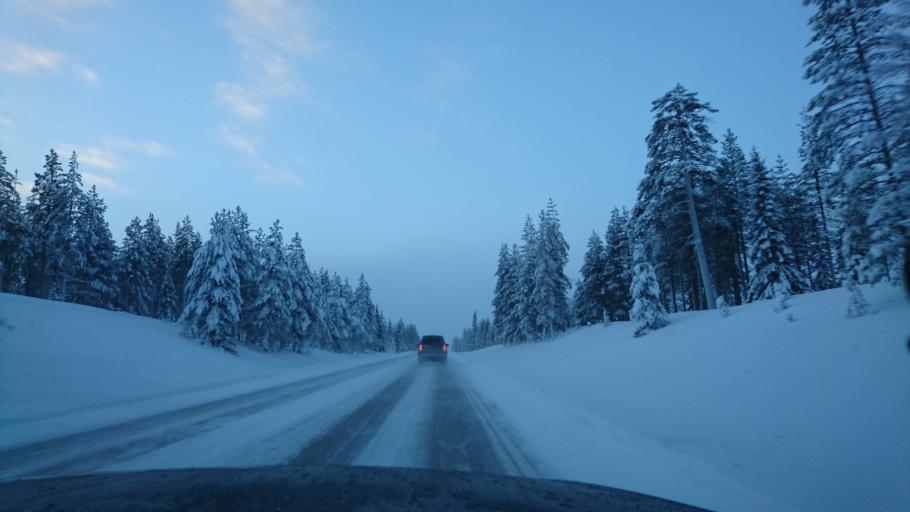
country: FI
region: Northern Ostrobothnia
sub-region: Koillismaa
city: Taivalkoski
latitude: 65.4734
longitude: 27.7419
